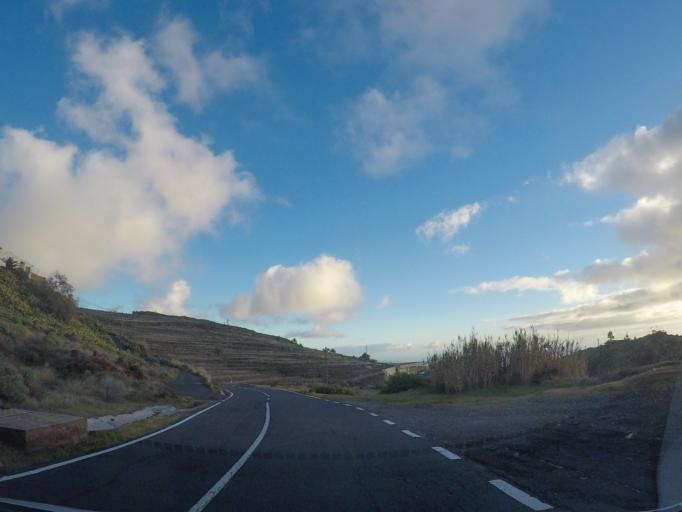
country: ES
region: Canary Islands
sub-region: Provincia de Santa Cruz de Tenerife
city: Alajero
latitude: 28.0726
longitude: -17.2383
